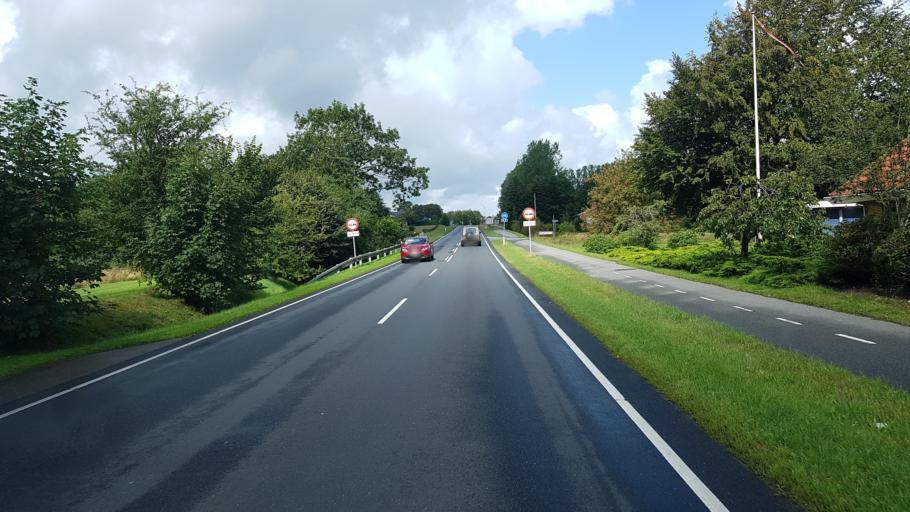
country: DK
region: South Denmark
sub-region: Vejen Kommune
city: Vejen
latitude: 55.5201
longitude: 9.1203
